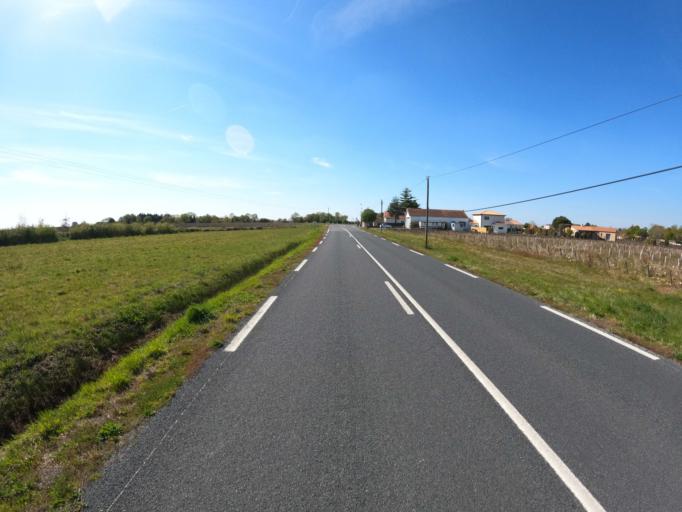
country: FR
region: Pays de la Loire
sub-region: Departement de la Loire-Atlantique
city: Gorges
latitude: 47.1126
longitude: -1.2906
